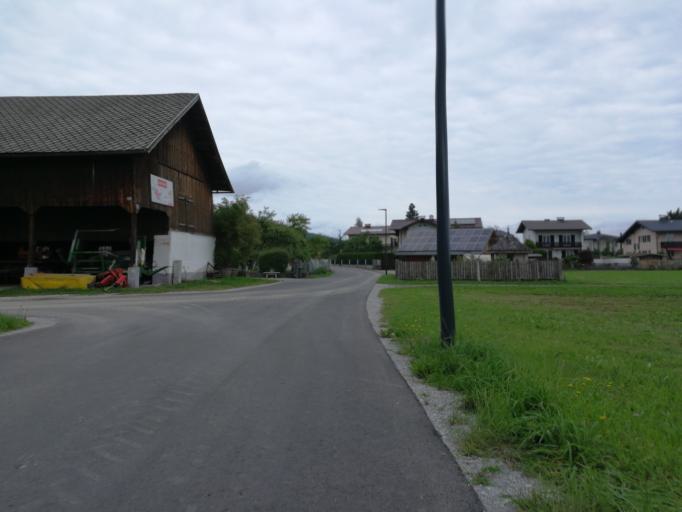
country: DE
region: Bavaria
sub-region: Upper Bavaria
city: Piding
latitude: 47.7748
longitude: 12.9553
